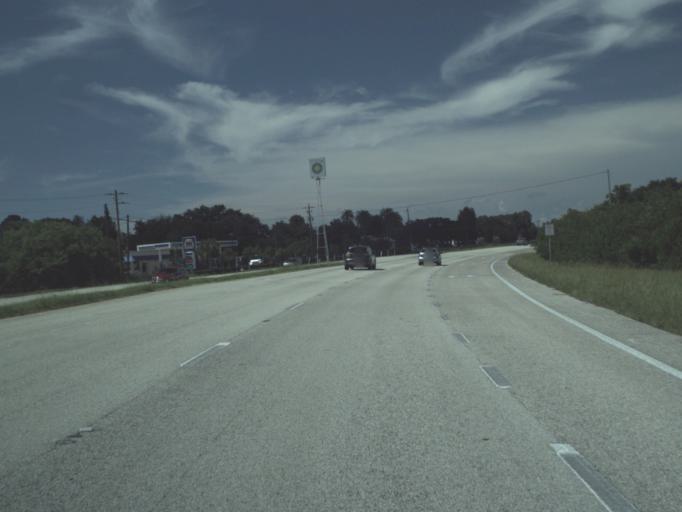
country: US
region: Florida
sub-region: Manatee County
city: Memphis
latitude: 27.5702
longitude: -82.5720
